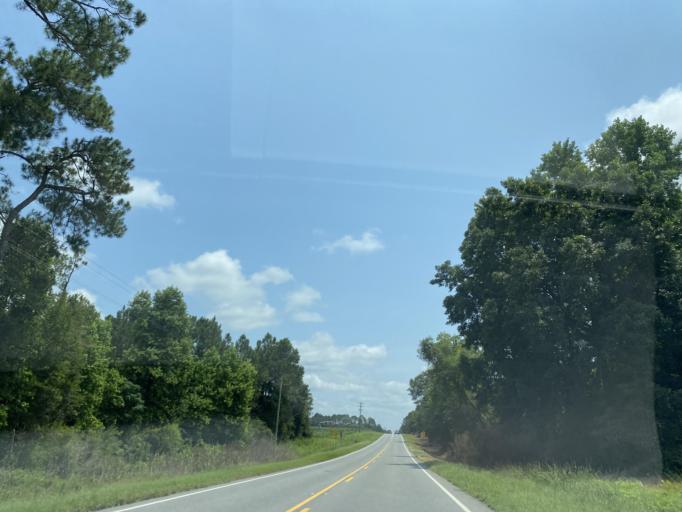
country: US
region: Georgia
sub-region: Jeff Davis County
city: Hazlehurst
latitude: 31.7553
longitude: -82.5494
